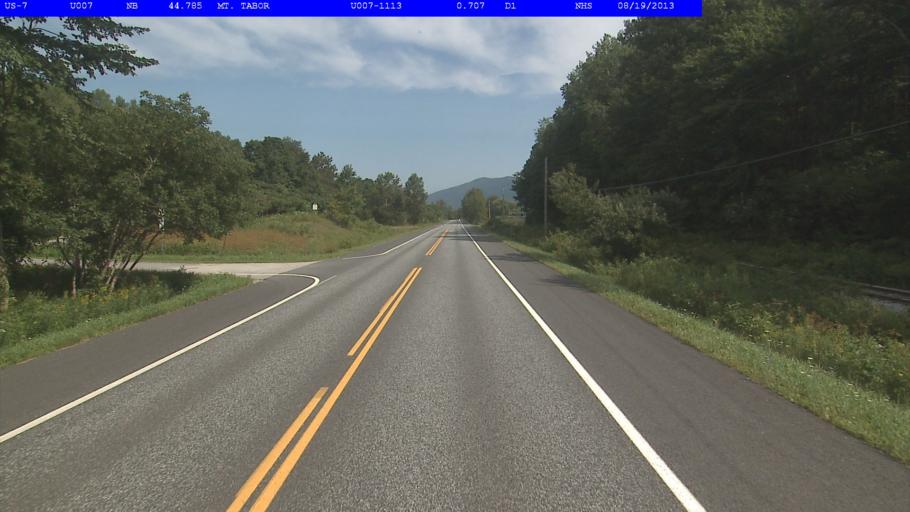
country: US
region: Vermont
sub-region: Bennington County
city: Manchester Center
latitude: 43.3151
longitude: -72.9922
